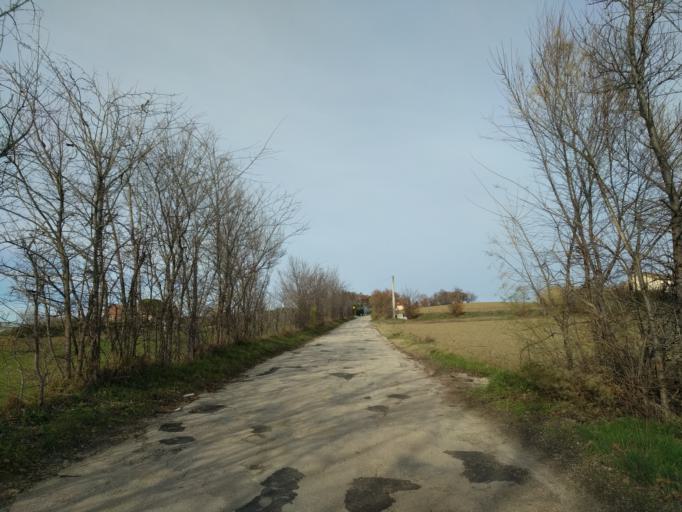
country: IT
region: The Marches
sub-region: Provincia di Pesaro e Urbino
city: Cuccurano
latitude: 43.8016
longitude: 12.9430
